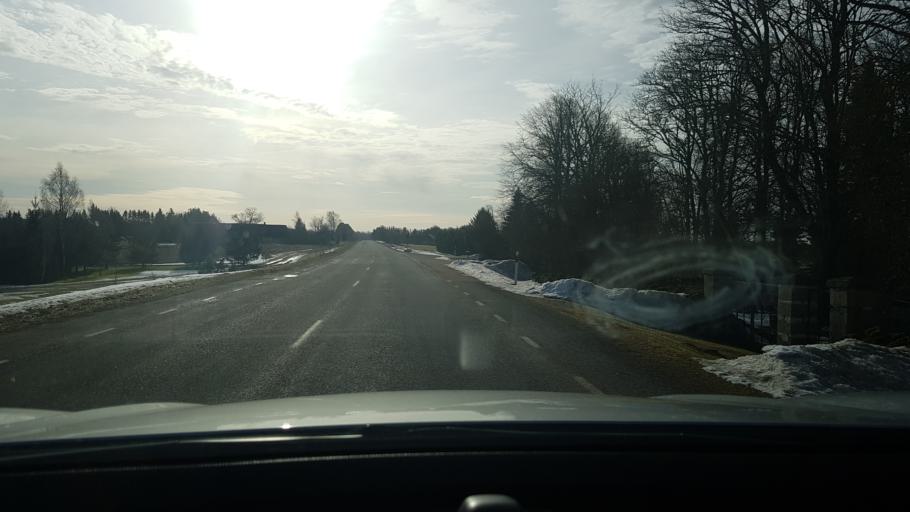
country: EE
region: Saare
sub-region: Kuressaare linn
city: Kuressaare
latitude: 58.5221
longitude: 22.7016
